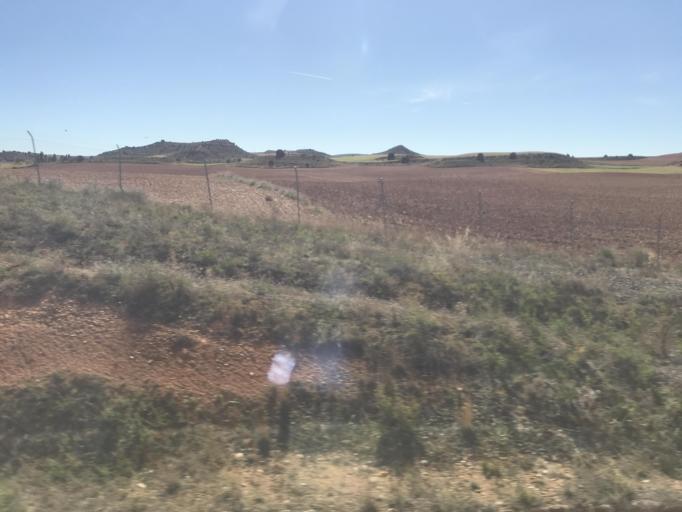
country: ES
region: Aragon
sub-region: Provincia de Zaragoza
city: Alconchel de Ariza
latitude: 41.2224
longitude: -2.0913
